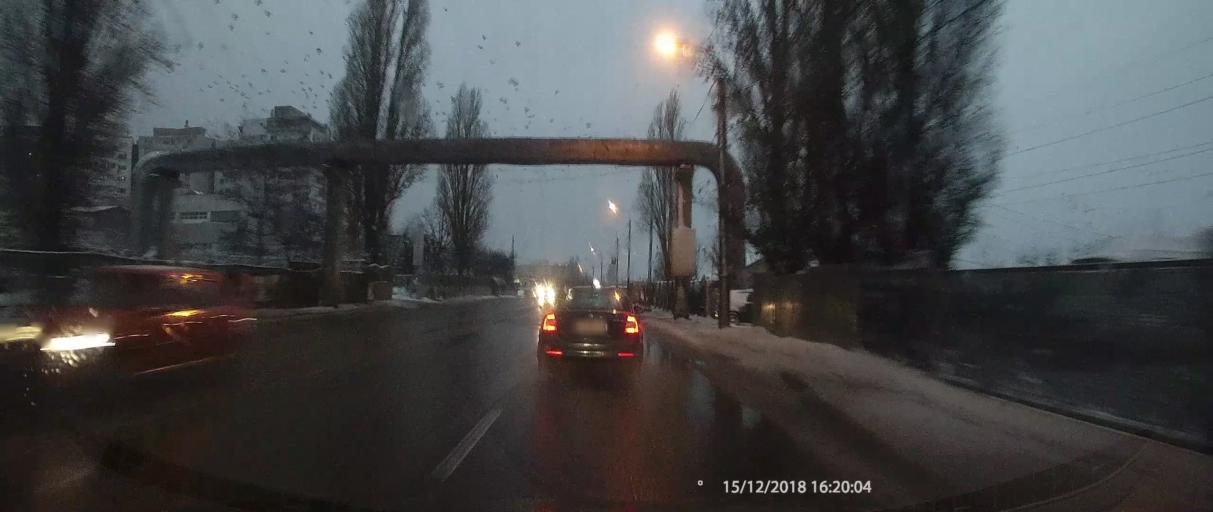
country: RO
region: Galati
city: Galati
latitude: 45.4153
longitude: 28.0049
